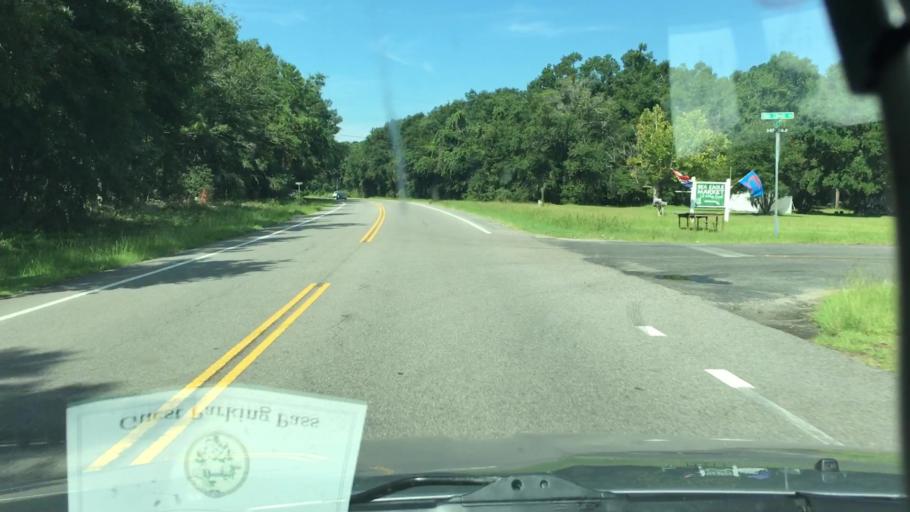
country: US
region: South Carolina
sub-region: Beaufort County
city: Beaufort
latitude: 32.4117
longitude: -80.5203
